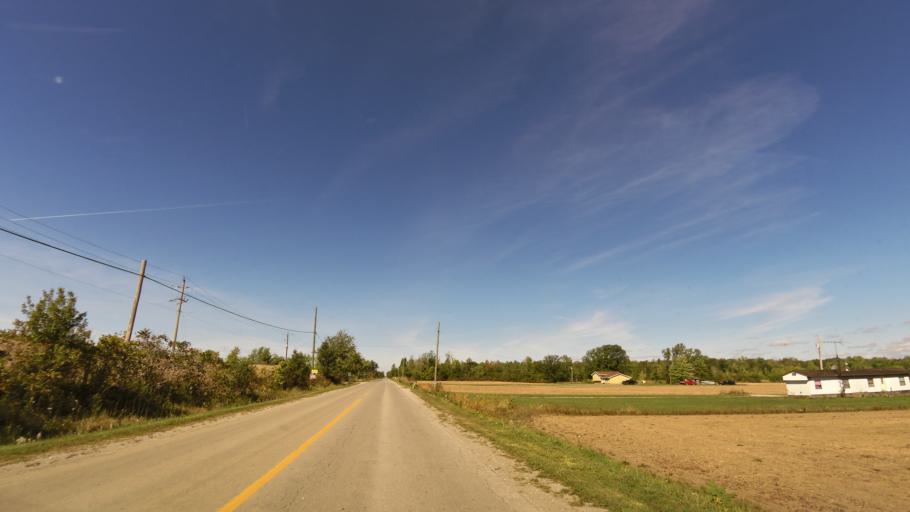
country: CA
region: Ontario
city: Ancaster
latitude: 43.0194
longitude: -80.0402
